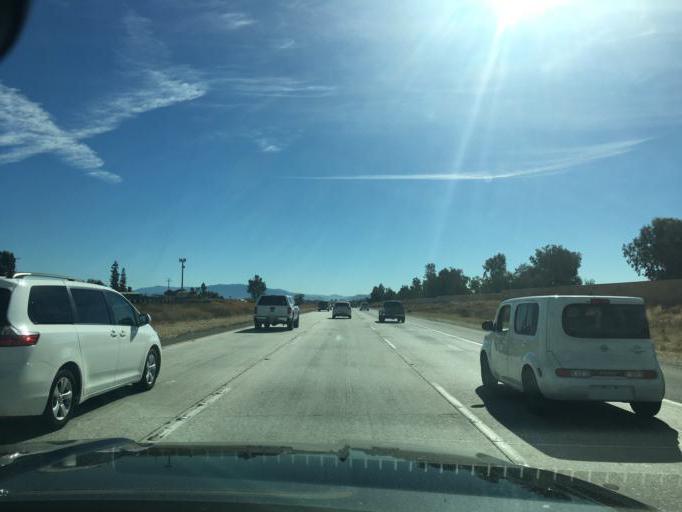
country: US
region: California
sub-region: Riverside County
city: Wildomar
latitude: 33.6081
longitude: -117.2565
